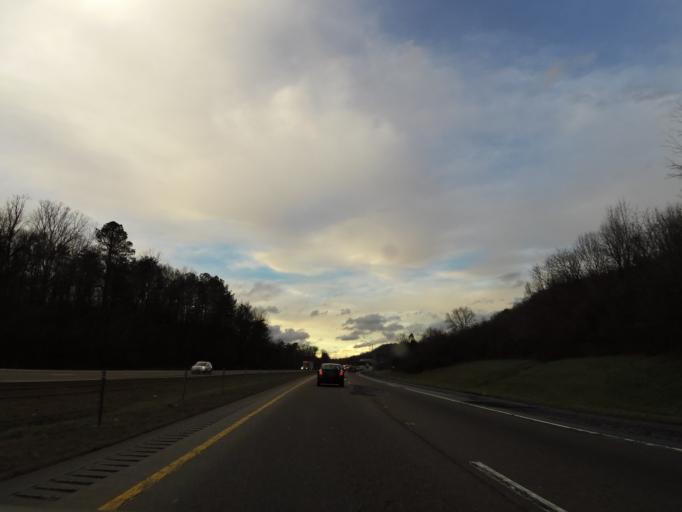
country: US
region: Tennessee
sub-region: Anderson County
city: Rocky Top
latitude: 36.2207
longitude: -84.1480
